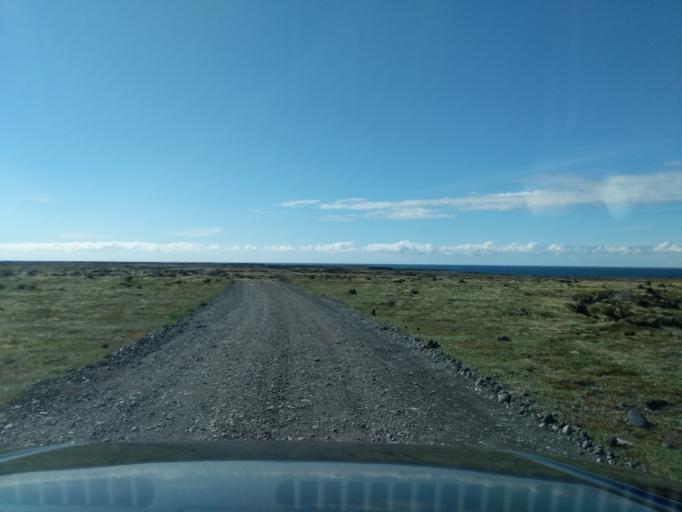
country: IS
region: West
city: Olafsvik
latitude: 64.8739
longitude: -24.0086
